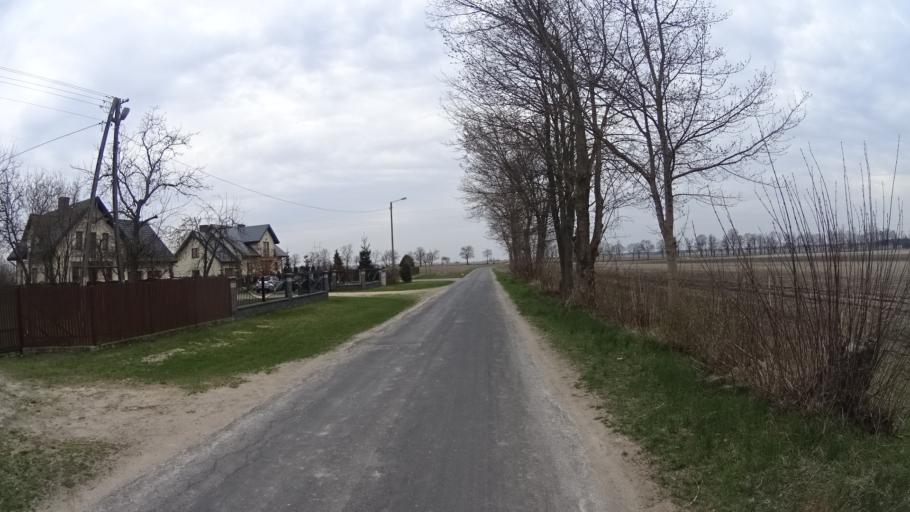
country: PL
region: Masovian Voivodeship
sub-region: Powiat warszawski zachodni
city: Blonie
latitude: 52.2478
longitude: 20.6529
